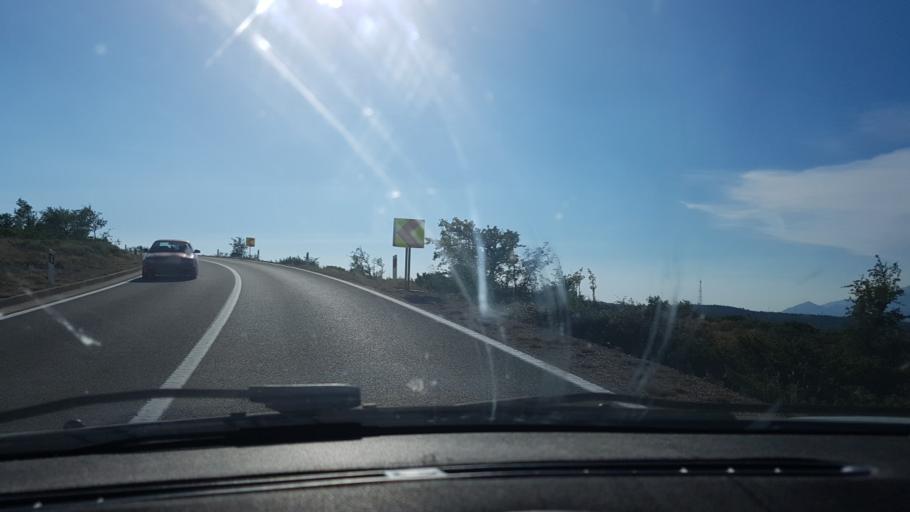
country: HR
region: Zadarska
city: Pridraga
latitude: 44.2288
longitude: 15.5937
